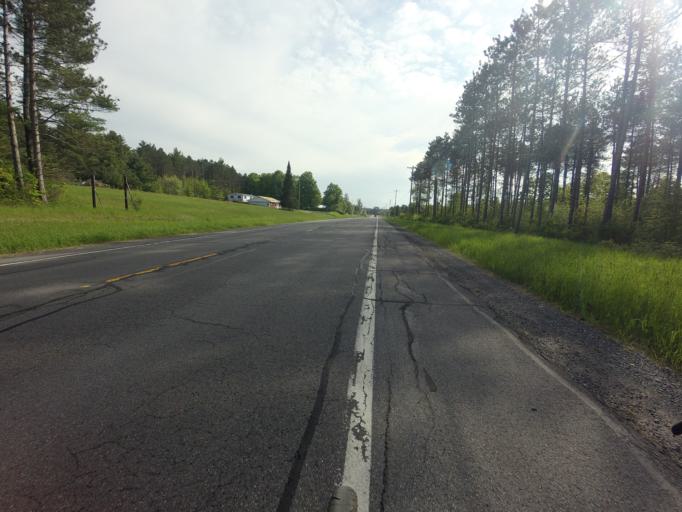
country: US
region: New York
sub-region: St. Lawrence County
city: Gouverneur
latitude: 44.1772
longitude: -75.2906
